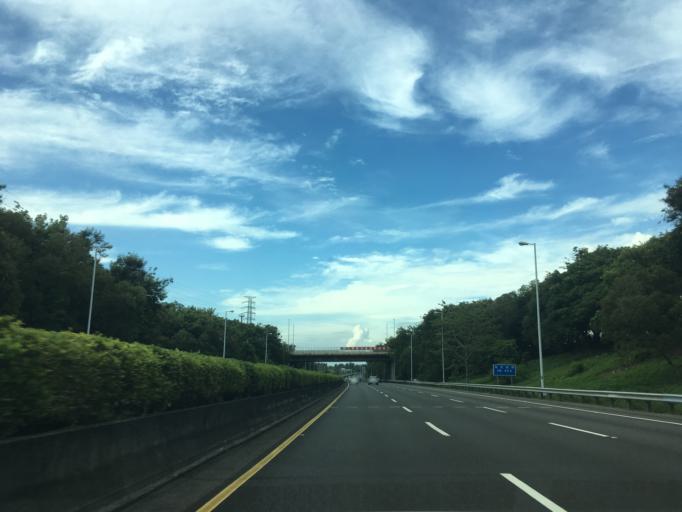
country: TW
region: Taiwan
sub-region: Yunlin
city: Douliu
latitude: 23.5935
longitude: 120.5217
